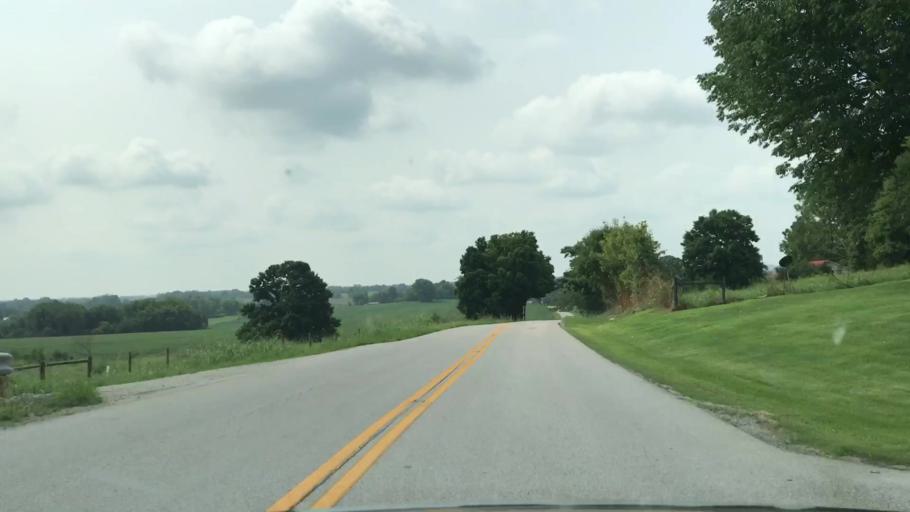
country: US
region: Kentucky
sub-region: Edmonson County
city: Brownsville
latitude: 37.1003
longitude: -86.1469
